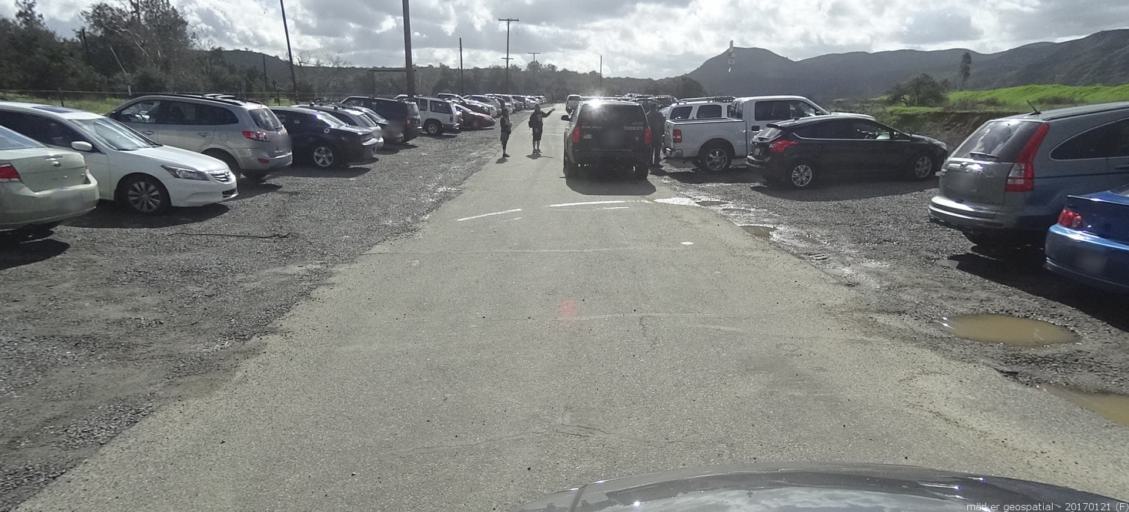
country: US
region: California
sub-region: Orange County
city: Foothill Ranch
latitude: 33.7642
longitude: -117.6780
